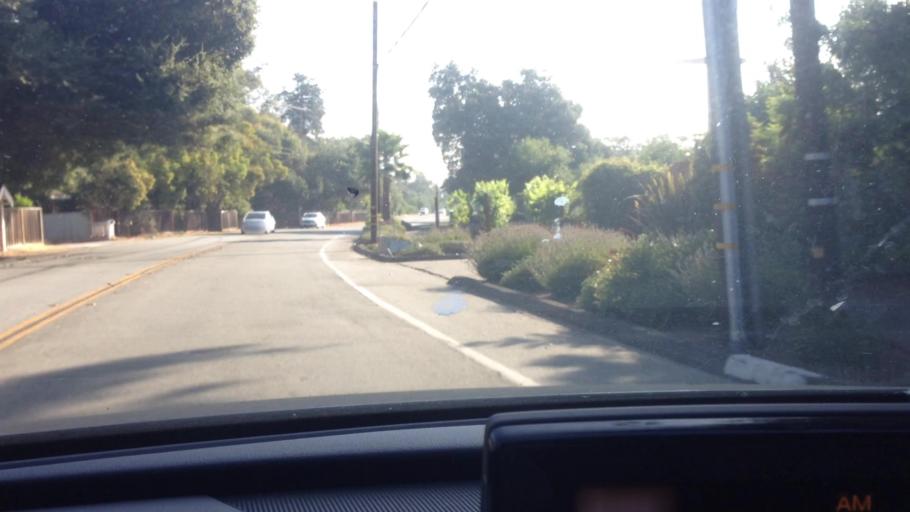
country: US
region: California
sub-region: Santa Clara County
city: Saratoga
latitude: 37.2680
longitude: -122.0195
